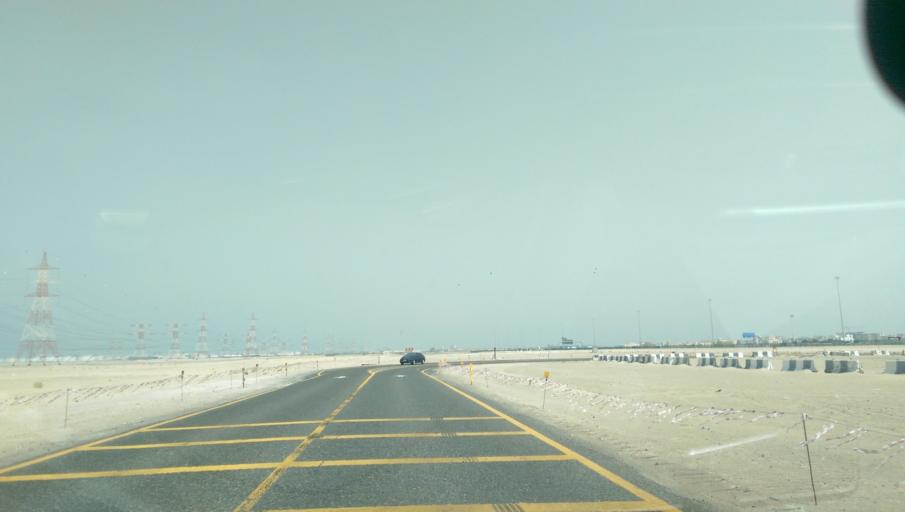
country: AE
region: Abu Dhabi
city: Abu Dhabi
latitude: 24.2977
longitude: 54.5387
